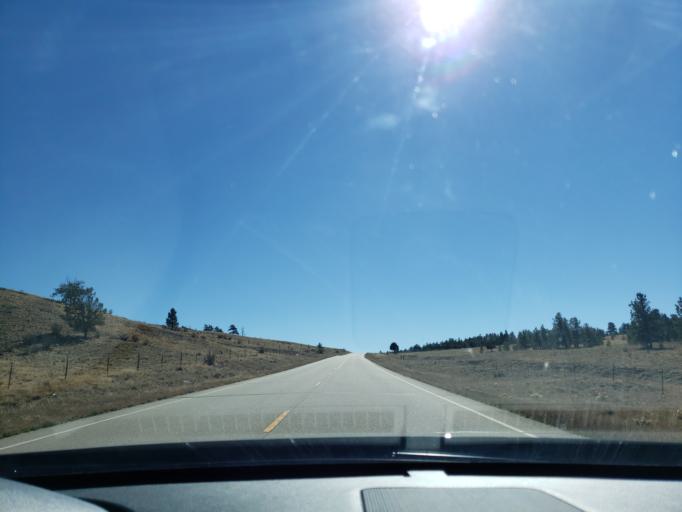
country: US
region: Colorado
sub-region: Park County
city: Fairplay
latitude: 38.9135
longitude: -105.7034
